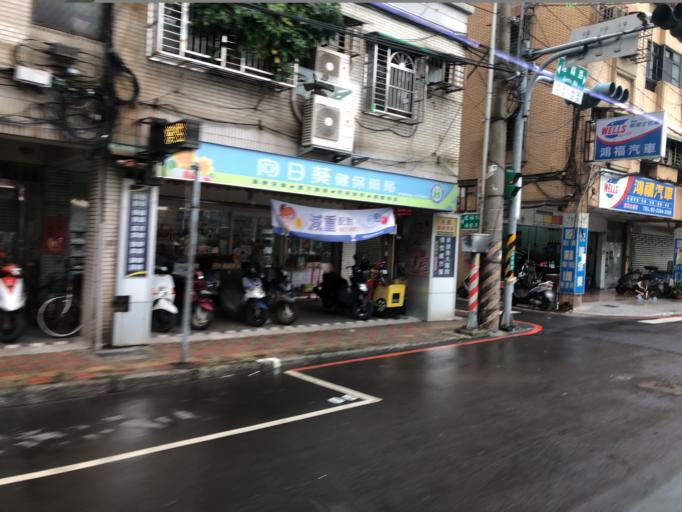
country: TW
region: Taipei
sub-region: Taipei
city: Banqiao
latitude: 25.0274
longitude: 121.4267
